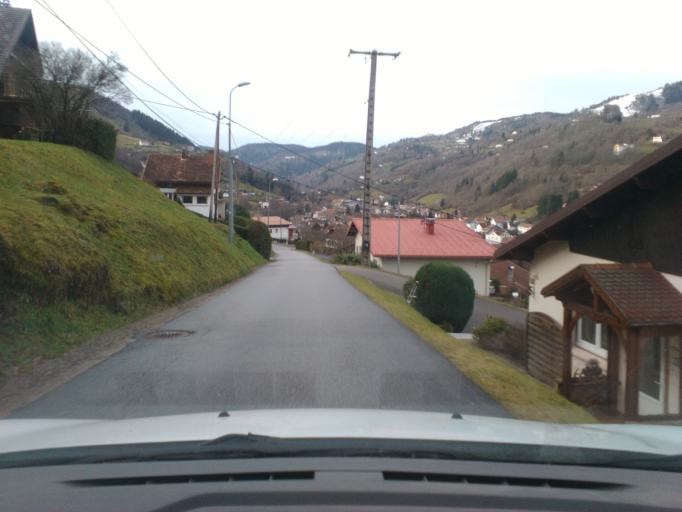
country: FR
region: Lorraine
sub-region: Departement des Vosges
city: La Bresse
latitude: 48.0024
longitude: 6.8776
